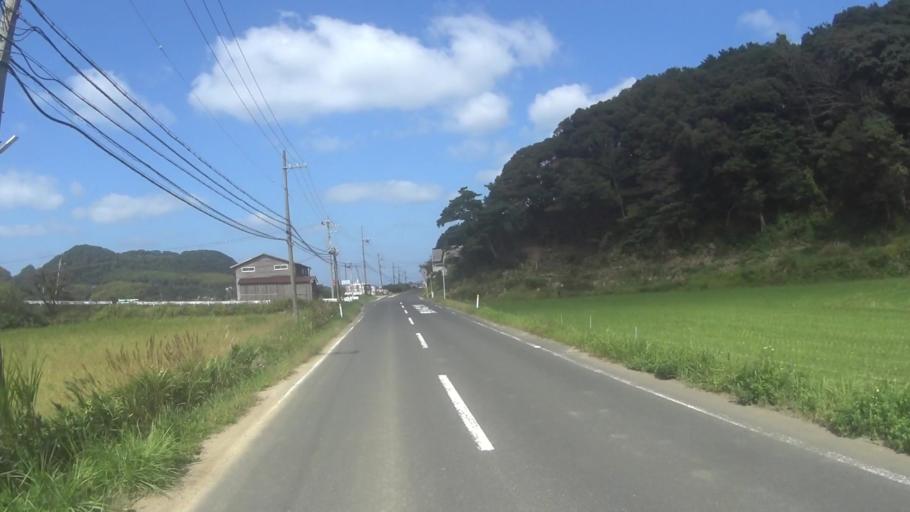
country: JP
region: Kyoto
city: Miyazu
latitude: 35.7284
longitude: 135.1036
